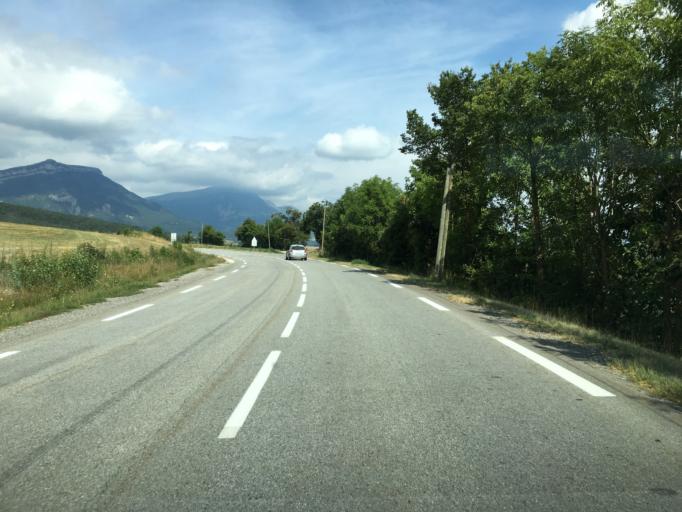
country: FR
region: Rhone-Alpes
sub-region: Departement de l'Isere
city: Mens
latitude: 44.8019
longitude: 5.6375
